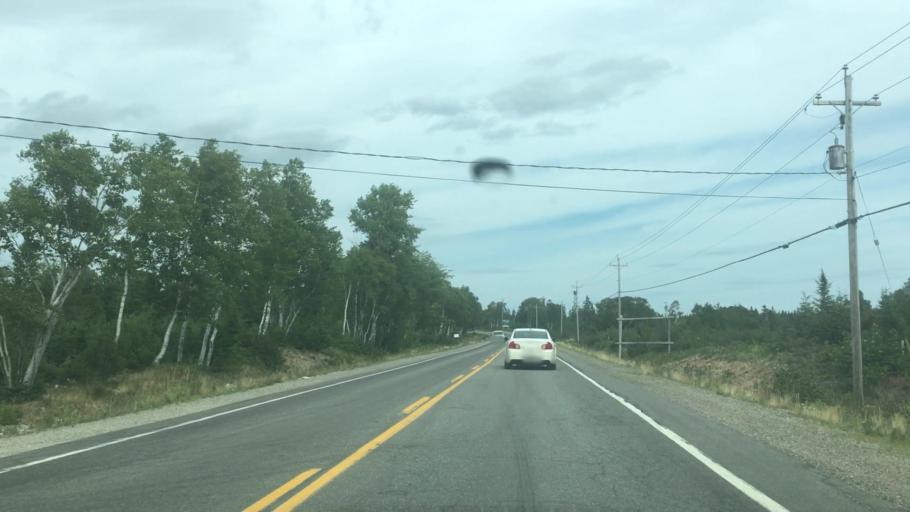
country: CA
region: Nova Scotia
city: Sydney Mines
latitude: 46.5161
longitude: -60.4267
